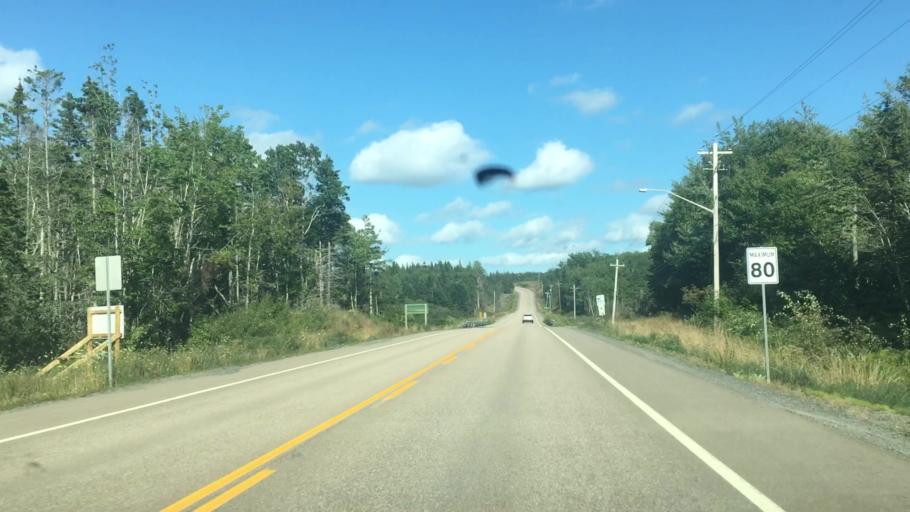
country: CA
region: Nova Scotia
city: Princeville
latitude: 45.6921
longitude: -60.7462
